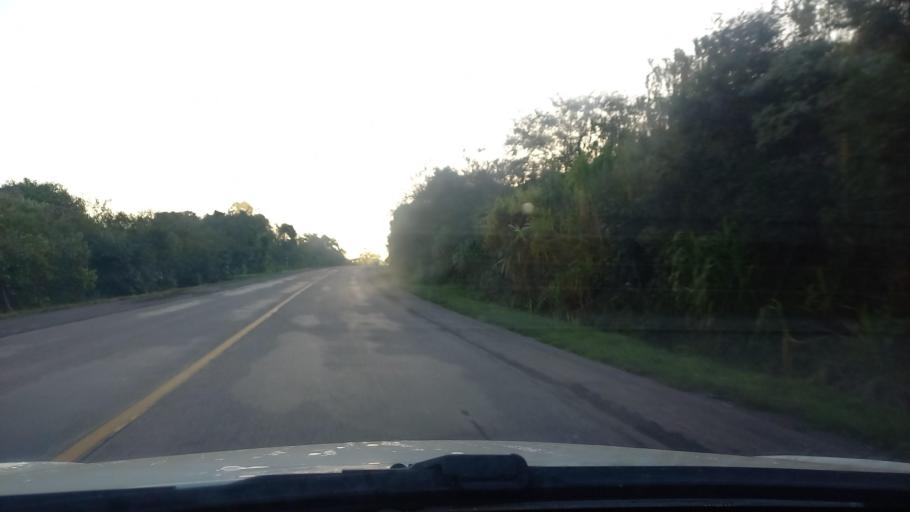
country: BR
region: Rio Grande do Sul
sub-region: Candelaria
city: Candelaria
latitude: -29.6839
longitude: -52.8451
